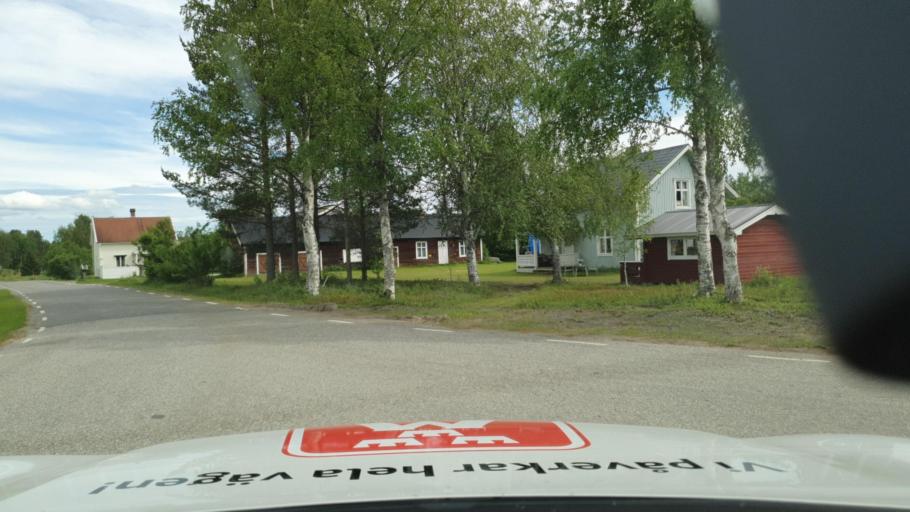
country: SE
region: Vaesterbotten
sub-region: Skelleftea Kommun
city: Burtraesk
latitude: 64.4974
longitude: 20.8584
